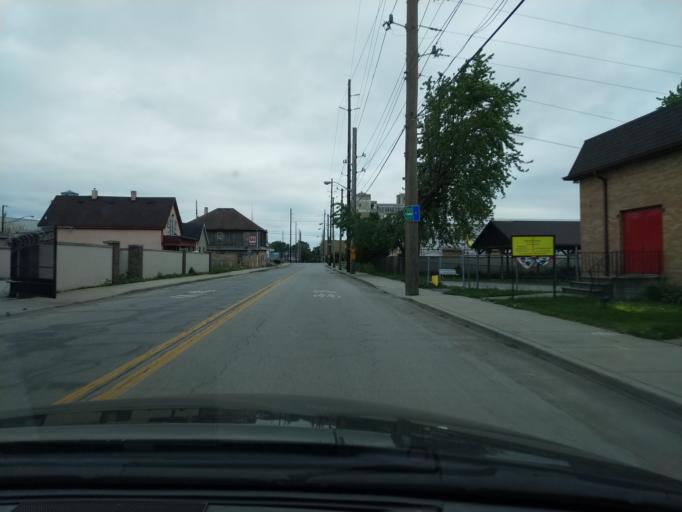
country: US
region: Indiana
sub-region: Marion County
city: Indianapolis
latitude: 39.7426
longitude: -86.1494
